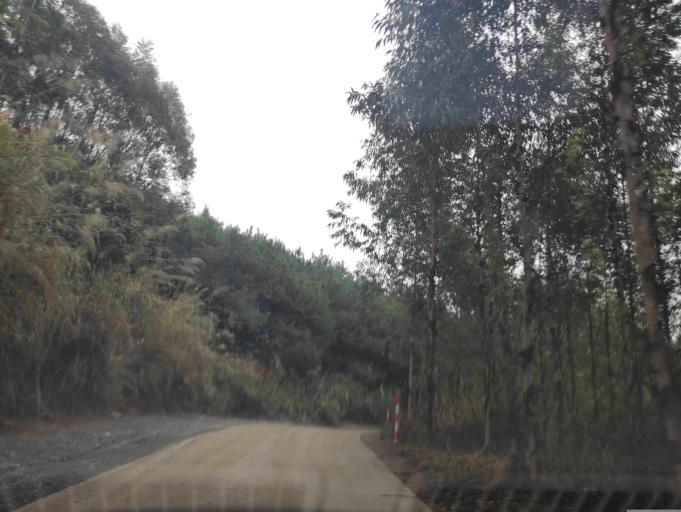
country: CN
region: Guangxi Zhuangzu Zizhiqu
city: Baise City
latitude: 23.8553
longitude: 106.7549
